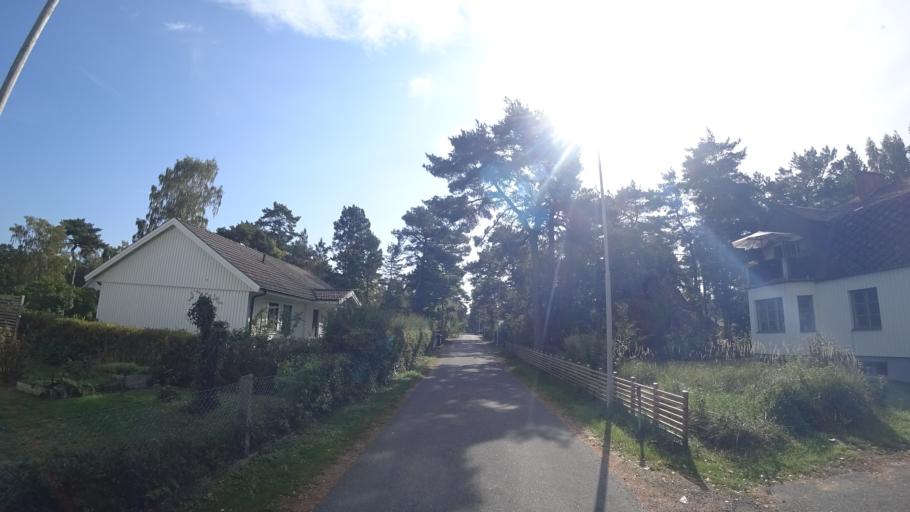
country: SE
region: Skane
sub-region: Kristianstads Kommun
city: Ahus
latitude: 55.9188
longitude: 14.2978
